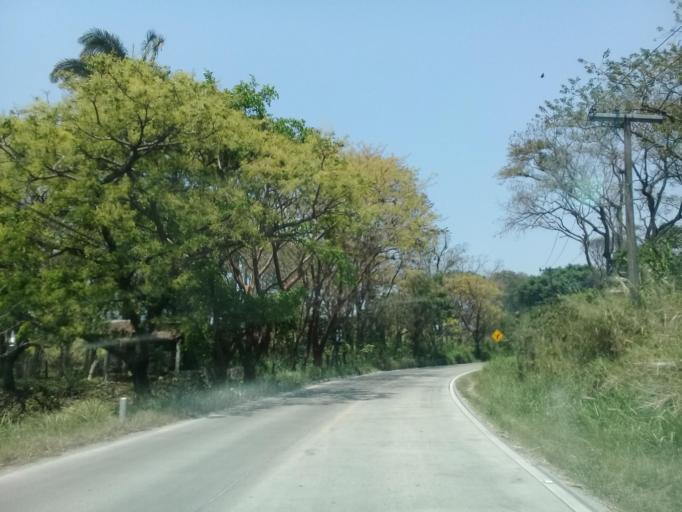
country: MX
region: Veracruz
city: Paraje Nuevo
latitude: 18.8710
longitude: -96.8764
